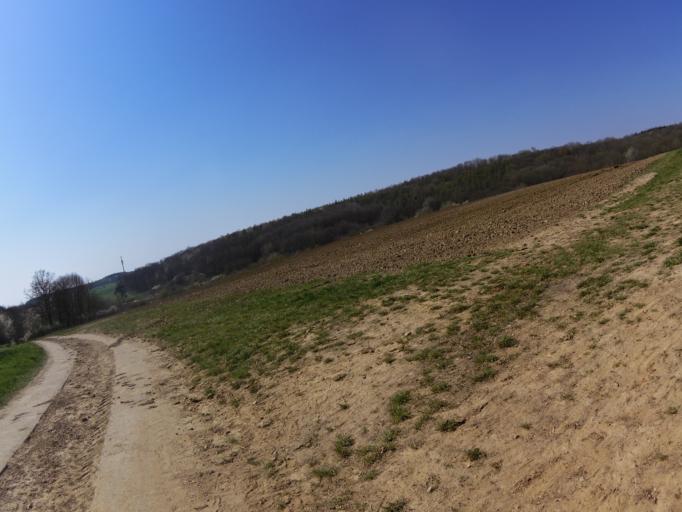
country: DE
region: Bavaria
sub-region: Regierungsbezirk Unterfranken
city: Rottendorf
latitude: 49.8181
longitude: 10.0707
